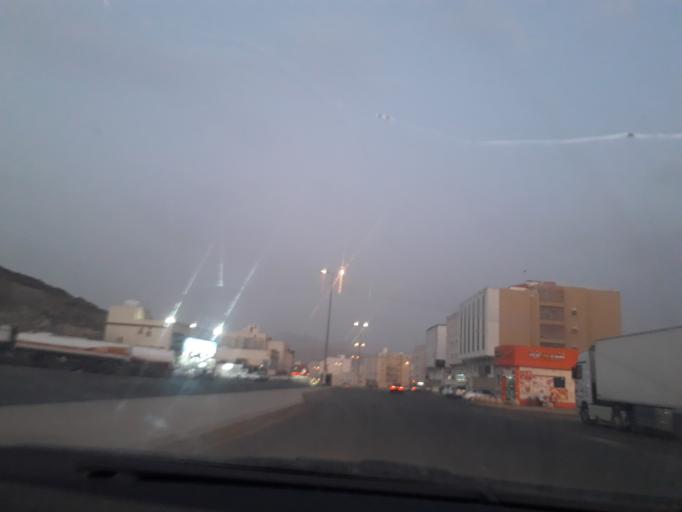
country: SA
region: Makkah
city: Mecca
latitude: 21.3810
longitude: 39.7781
